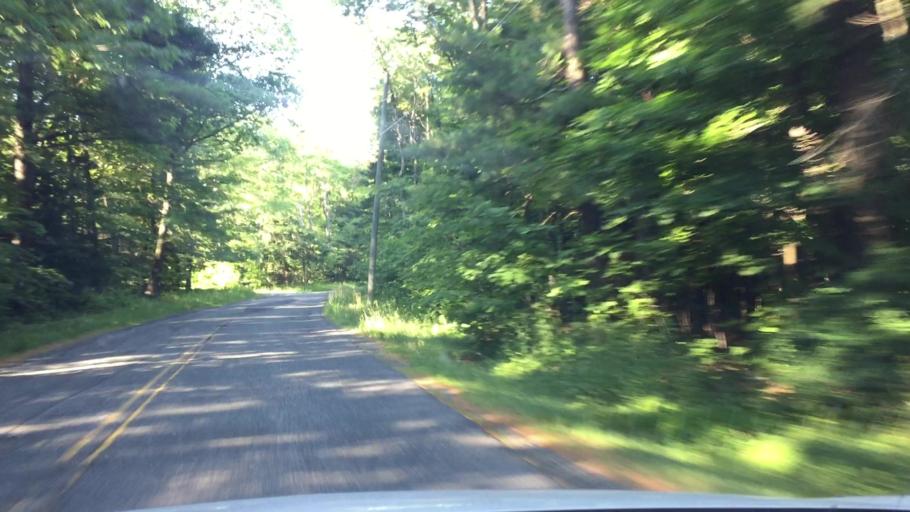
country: US
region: Massachusetts
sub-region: Berkshire County
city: Becket
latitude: 42.3046
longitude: -73.1307
